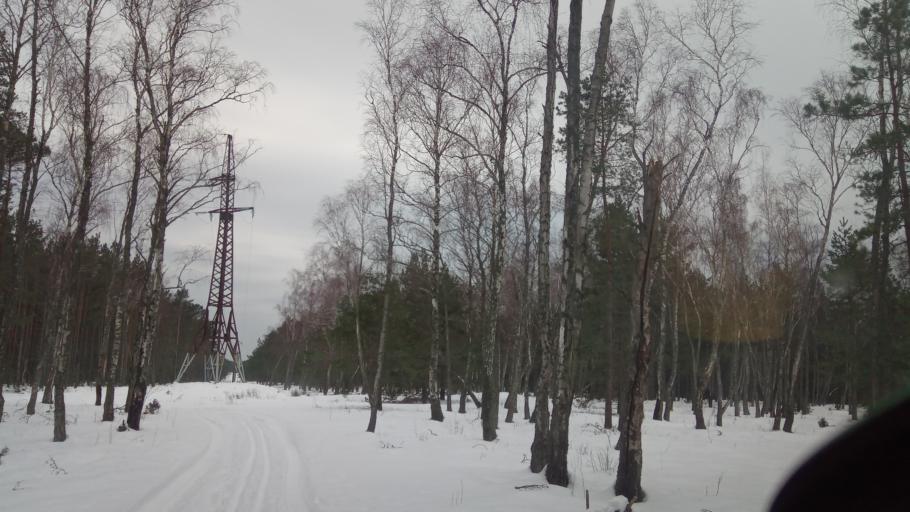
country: LT
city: Neringa
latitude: 55.4185
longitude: 21.0976
